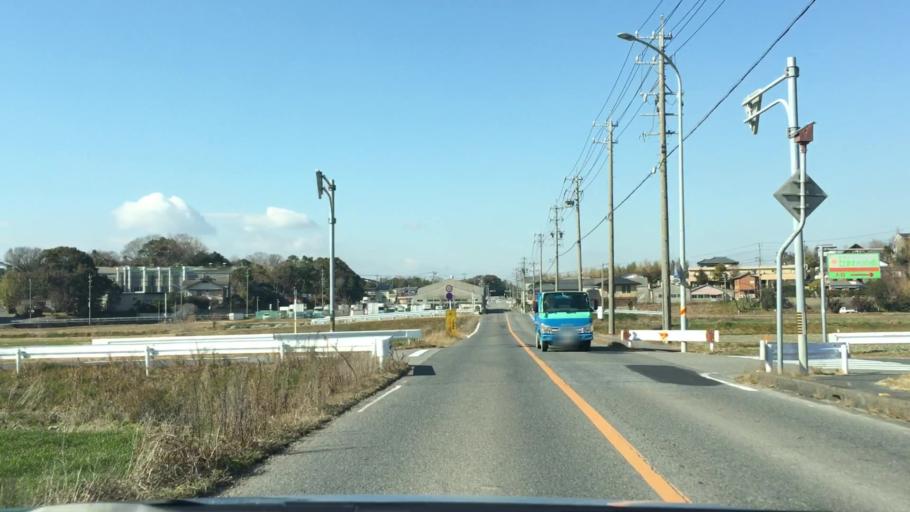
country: JP
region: Aichi
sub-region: Toyota-shi
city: Toyota
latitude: 35.0438
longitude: 137.1173
